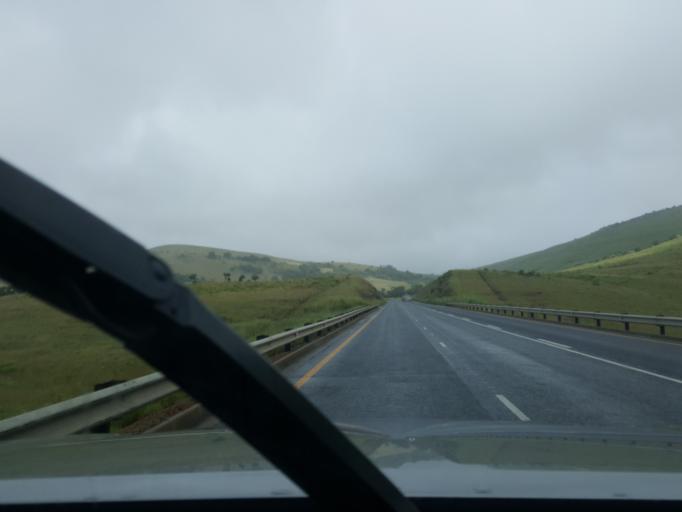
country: ZA
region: Mpumalanga
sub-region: Nkangala District Municipality
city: Belfast
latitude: -25.6260
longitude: 30.3347
